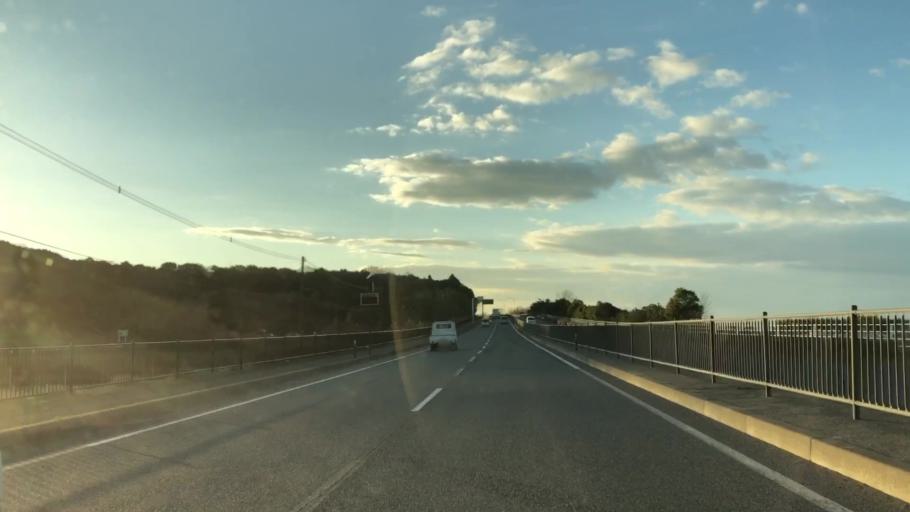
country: JP
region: Fukuoka
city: Nakatsu
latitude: 33.5536
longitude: 131.2582
